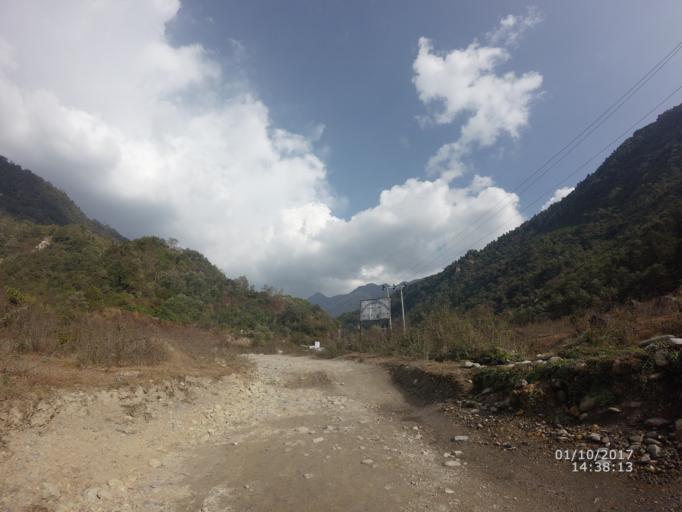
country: NP
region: Western Region
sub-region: Gandaki Zone
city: Pokhara
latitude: 28.3453
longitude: 83.9714
